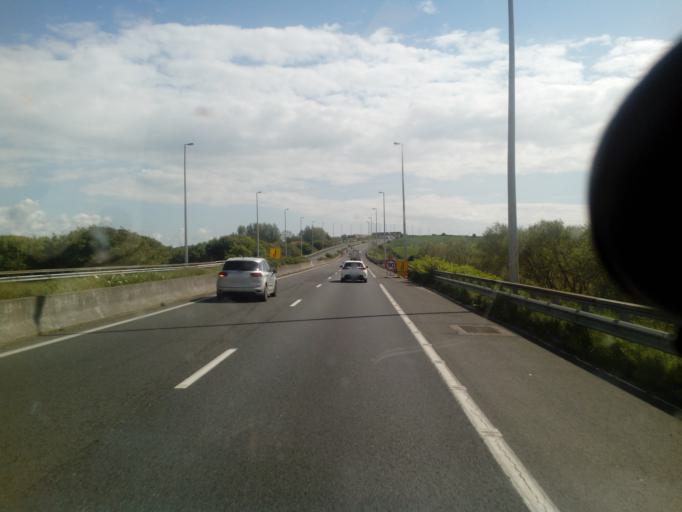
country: FR
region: Nord-Pas-de-Calais
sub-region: Departement du Pas-de-Calais
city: Marquise
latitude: 50.8003
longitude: 1.6900
